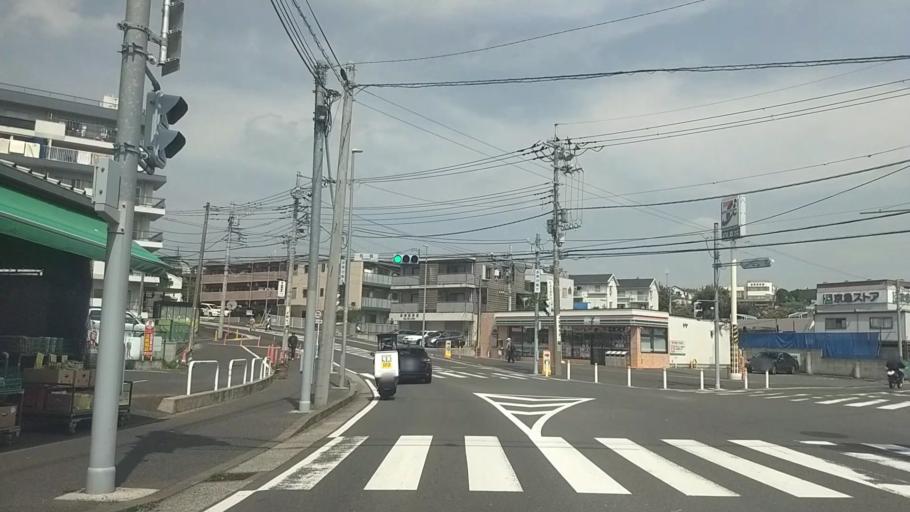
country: JP
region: Kanagawa
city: Yokohama
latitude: 35.4132
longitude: 139.6086
